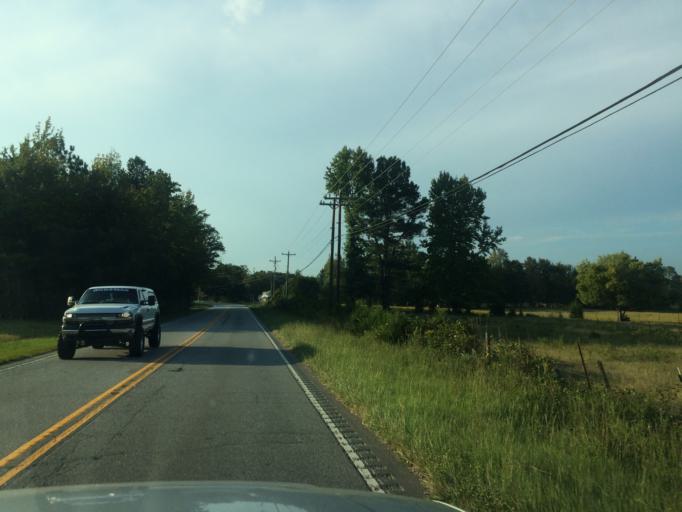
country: US
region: South Carolina
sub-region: Anderson County
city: Williamston
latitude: 34.6538
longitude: -82.4913
